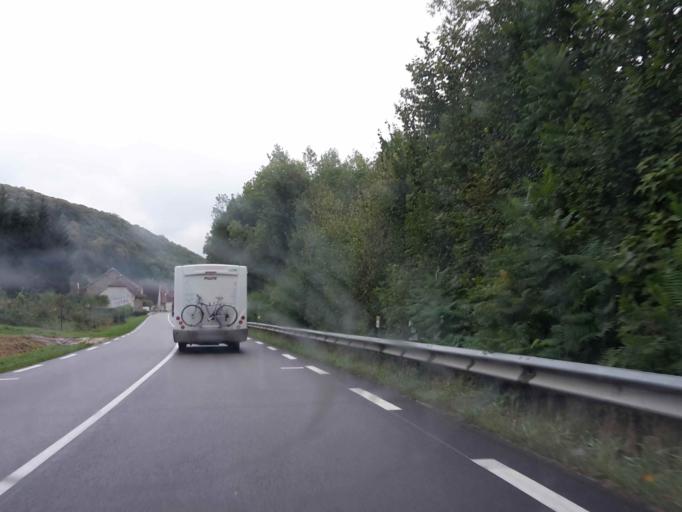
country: FR
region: Franche-Comte
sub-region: Departement du Doubs
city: Novillars
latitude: 47.3011
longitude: 6.1639
